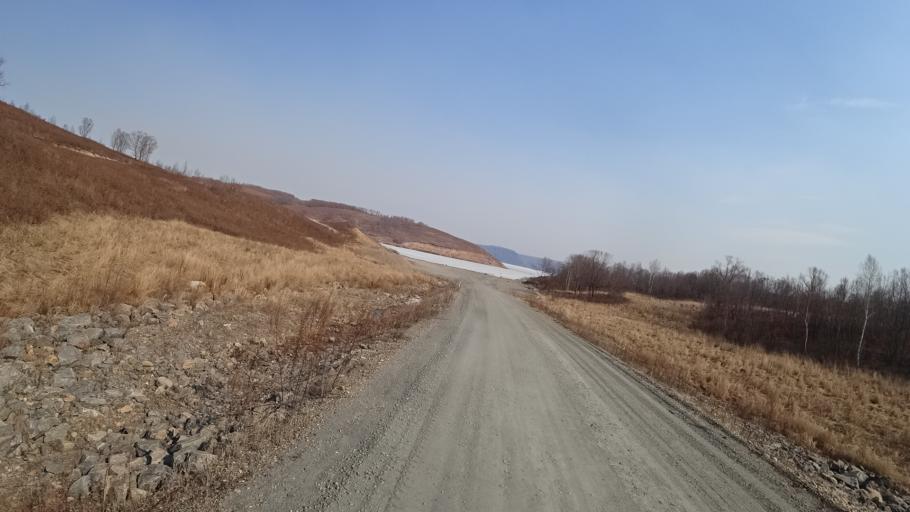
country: RU
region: Amur
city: Novobureyskiy
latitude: 49.8218
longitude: 129.9999
